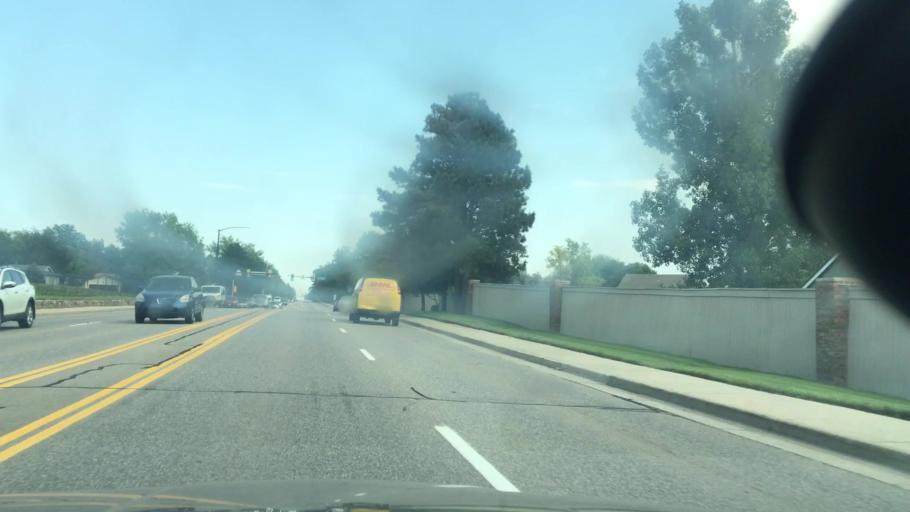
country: US
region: Colorado
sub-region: Arapahoe County
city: Castlewood
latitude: 39.5805
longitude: -104.8996
